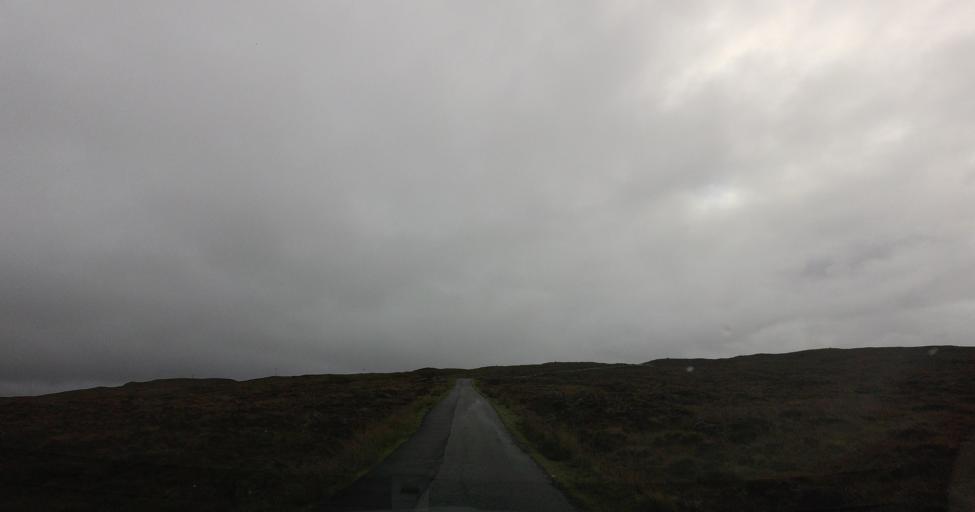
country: GB
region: Scotland
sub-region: Highland
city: Isle of Skye
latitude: 57.1460
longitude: -6.0940
